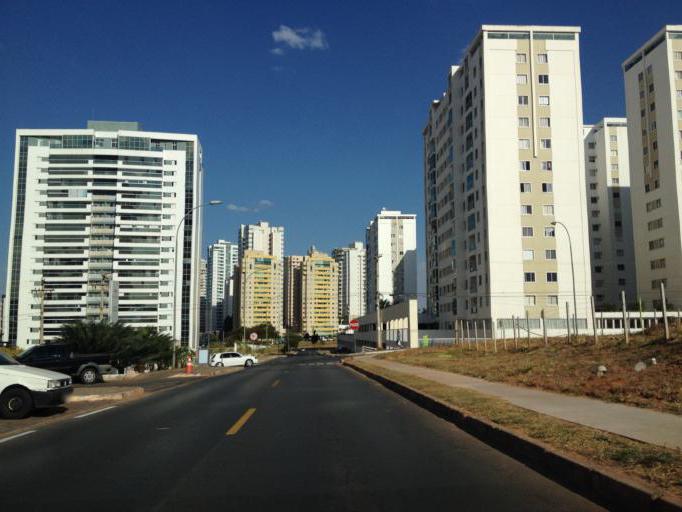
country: BR
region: Federal District
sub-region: Brasilia
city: Brasilia
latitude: -15.8324
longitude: -48.0355
